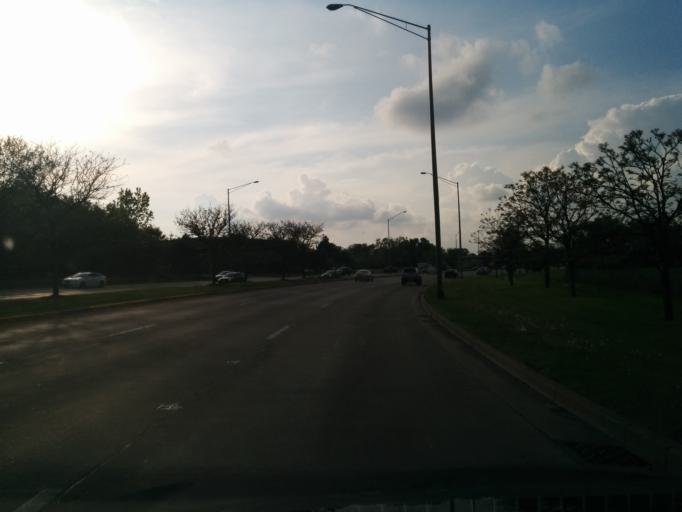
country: US
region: Illinois
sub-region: DuPage County
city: Hanover Park
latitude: 41.9832
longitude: -88.1414
